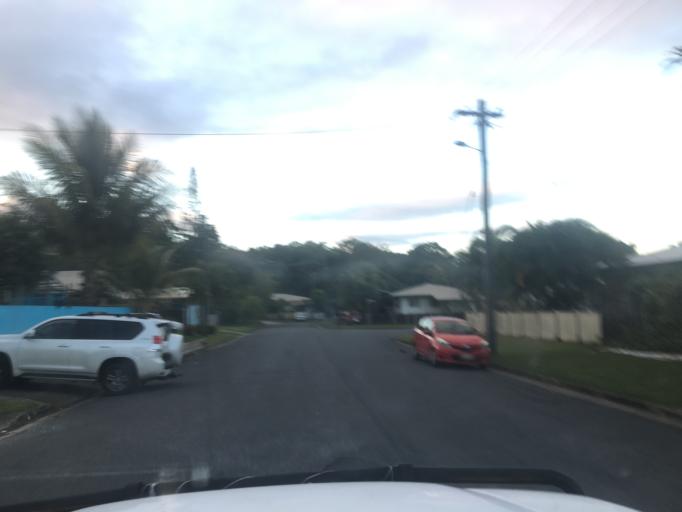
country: AU
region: Queensland
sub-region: Cairns
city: Woree
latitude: -16.9252
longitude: 145.7324
